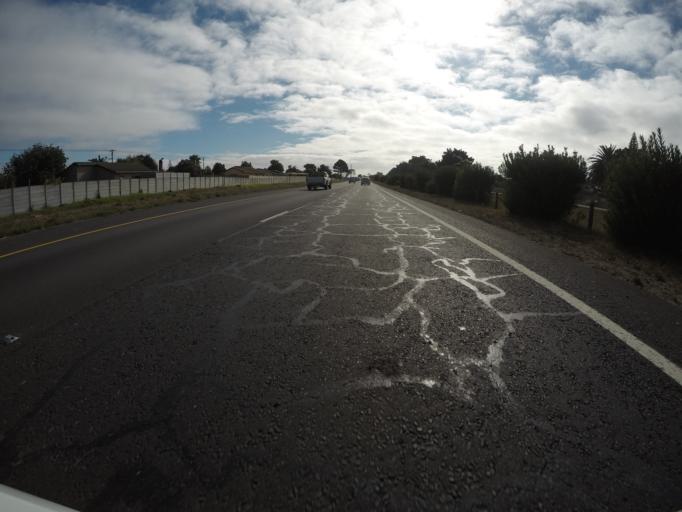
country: ZA
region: Western Cape
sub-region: City of Cape Town
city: Kraaifontein
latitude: -33.8414
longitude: 18.7209
